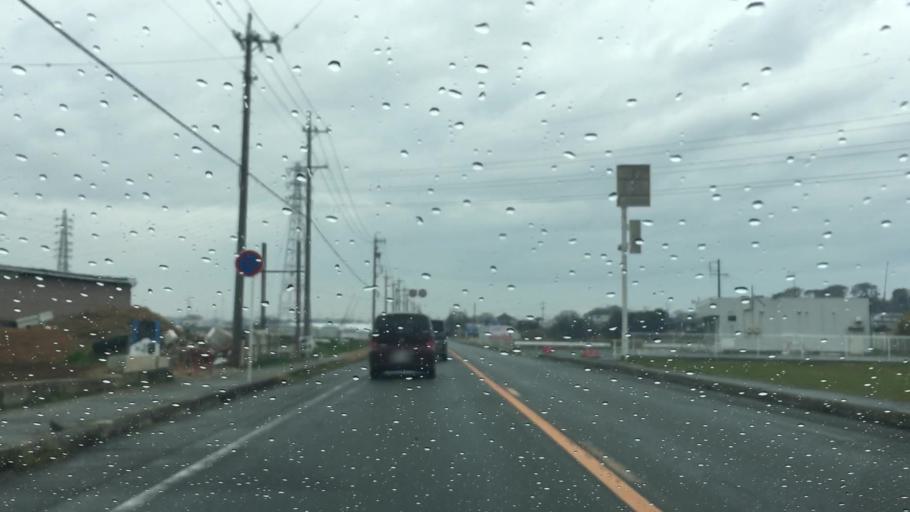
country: JP
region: Aichi
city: Toyohashi
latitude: 34.7150
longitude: 137.3940
